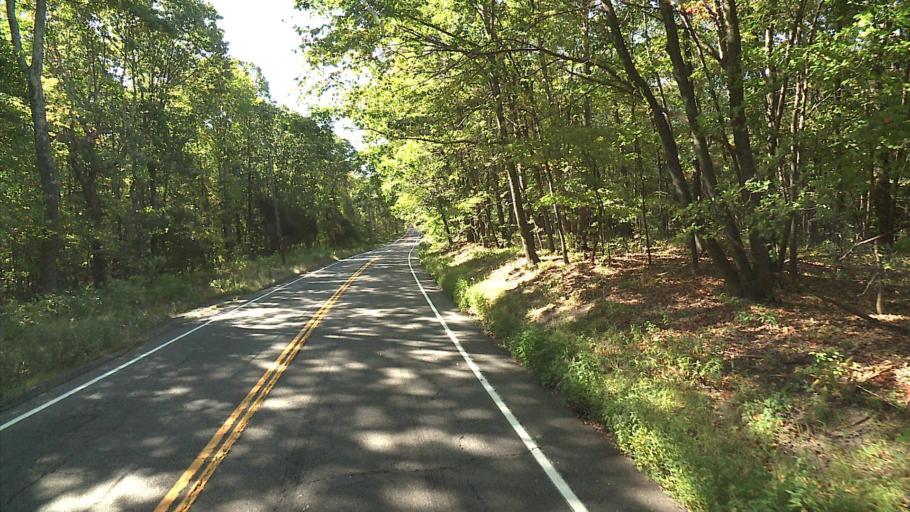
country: US
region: Connecticut
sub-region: Hartford County
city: Collinsville
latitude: 41.7596
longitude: -72.9757
